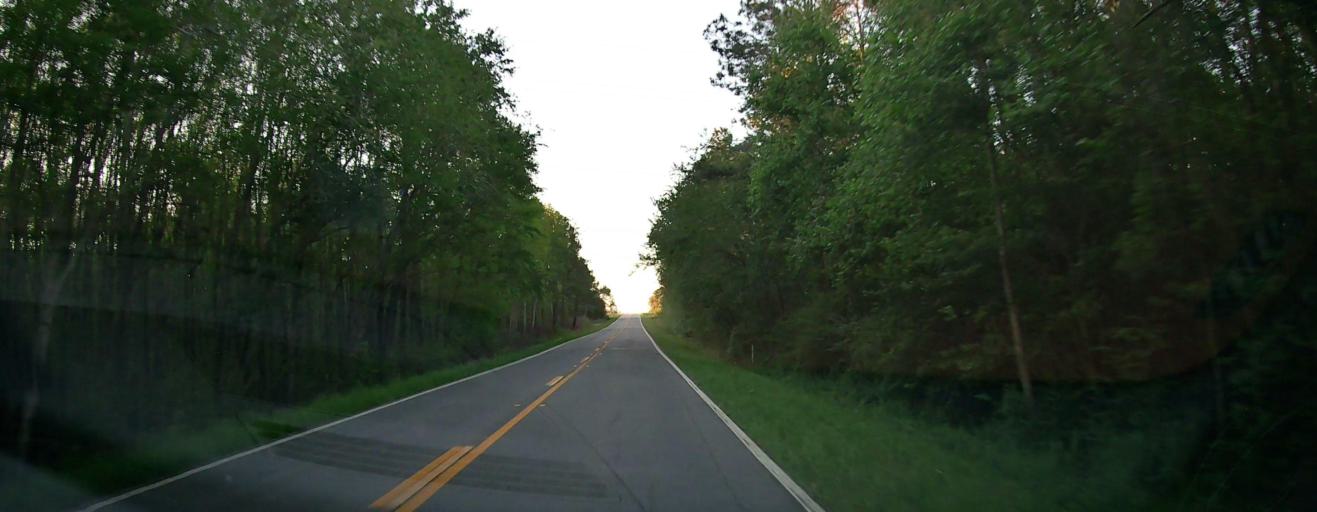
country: US
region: Georgia
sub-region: Ben Hill County
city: Fitzgerald
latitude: 31.7363
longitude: -83.3098
